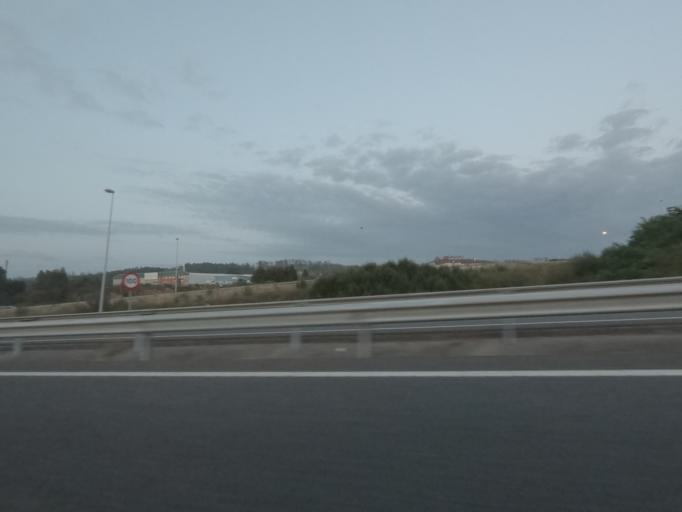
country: ES
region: Galicia
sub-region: Provincia de Pontevedra
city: Tui
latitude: 42.0837
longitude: -8.6280
